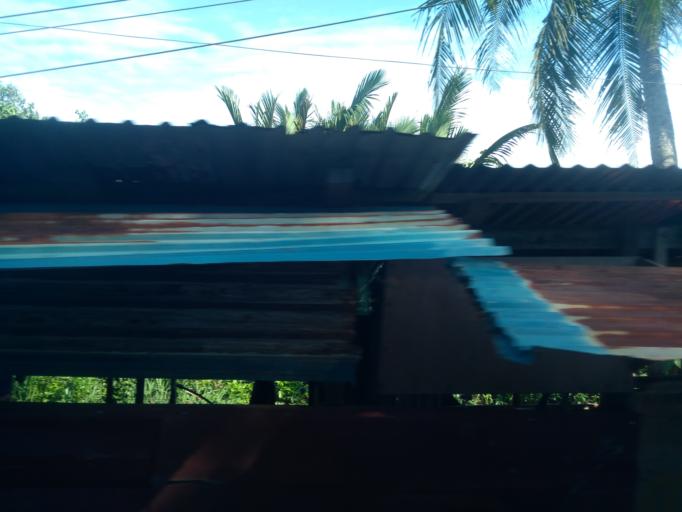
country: MY
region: Sarawak
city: Kuching
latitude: 1.6622
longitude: 110.4317
